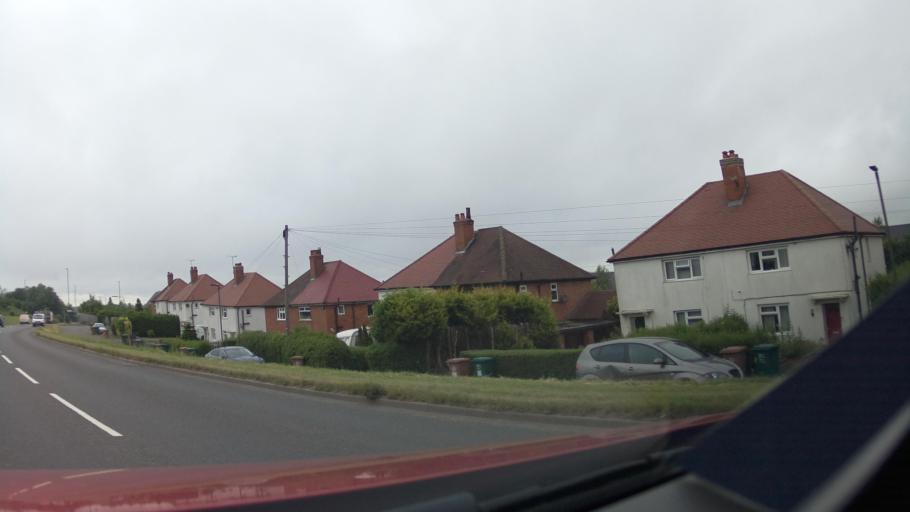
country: GB
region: England
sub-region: Derbyshire
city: Swadlincote
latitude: 52.7625
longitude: -1.5901
